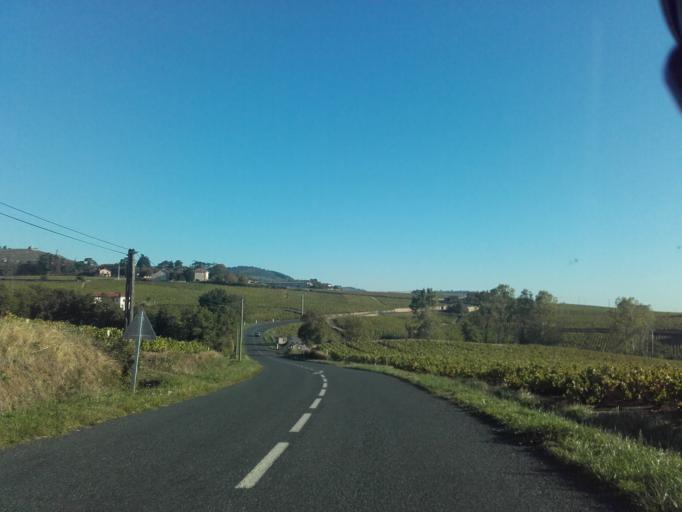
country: FR
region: Rhone-Alpes
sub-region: Departement du Rhone
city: Fleurie
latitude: 46.1780
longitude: 4.6925
